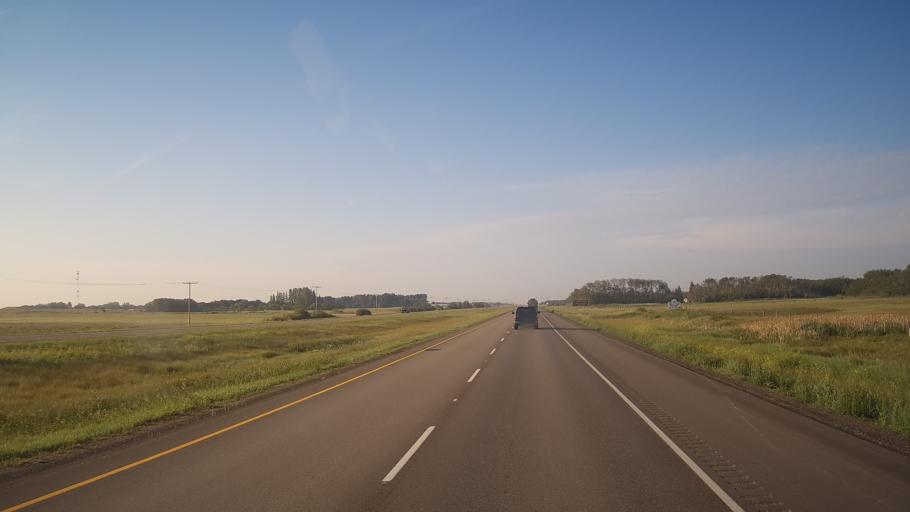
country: CA
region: Saskatchewan
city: Saskatoon
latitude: 51.9795
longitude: -106.5584
